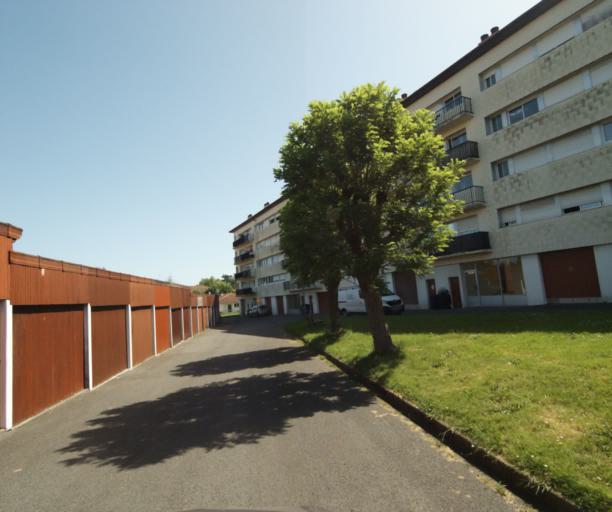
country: FR
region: Aquitaine
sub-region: Departement des Pyrenees-Atlantiques
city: Bayonne
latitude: 43.4781
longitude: -1.4610
